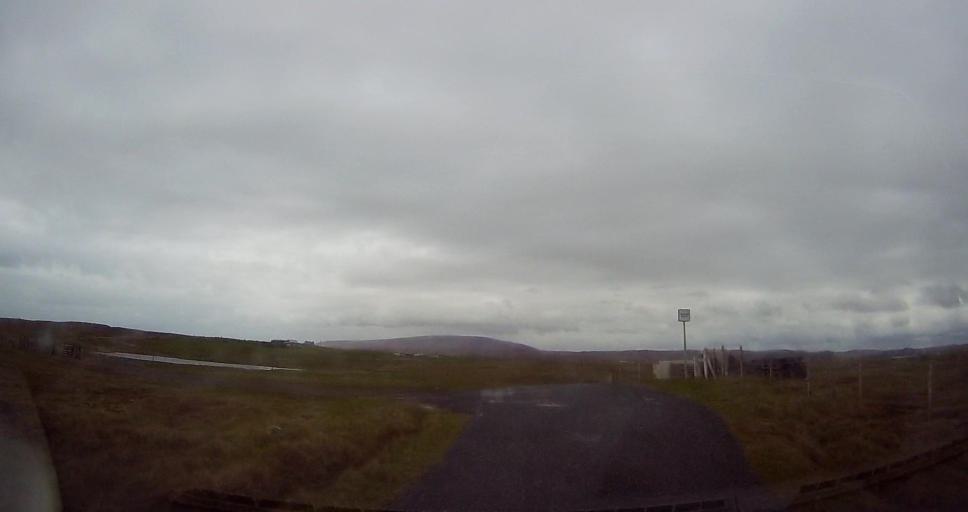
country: GB
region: Scotland
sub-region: Shetland Islands
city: Lerwick
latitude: 60.4807
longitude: -1.6102
